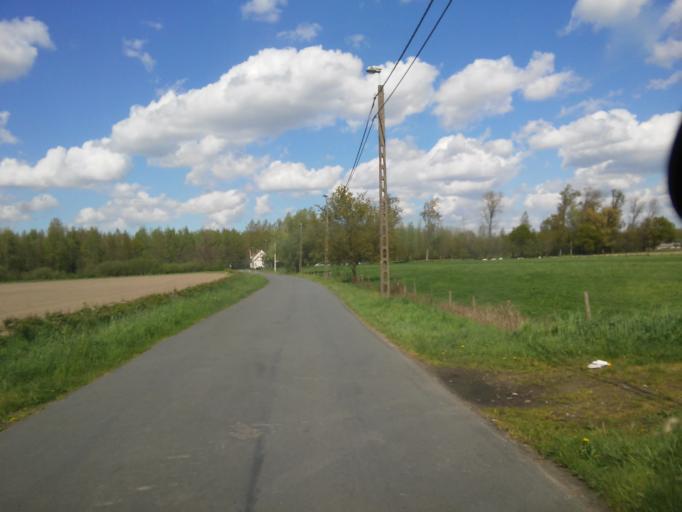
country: BE
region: Flanders
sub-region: Provincie Antwerpen
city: Puurs
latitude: 51.0843
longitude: 4.2892
